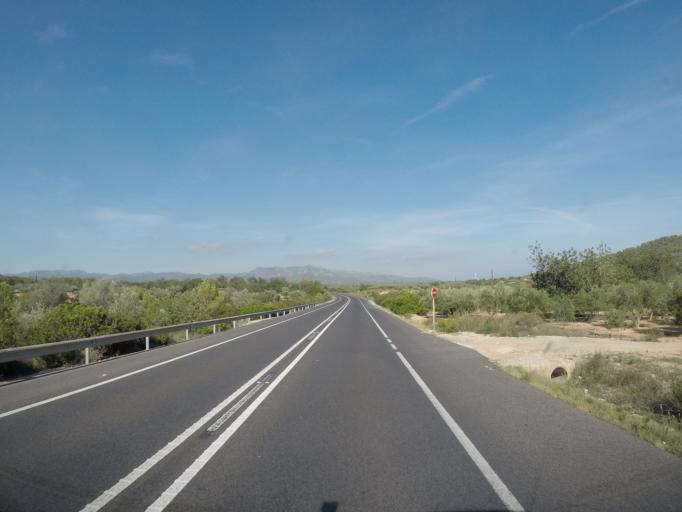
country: ES
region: Catalonia
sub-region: Provincia de Tarragona
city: El Perello
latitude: 40.8911
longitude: 0.7244
